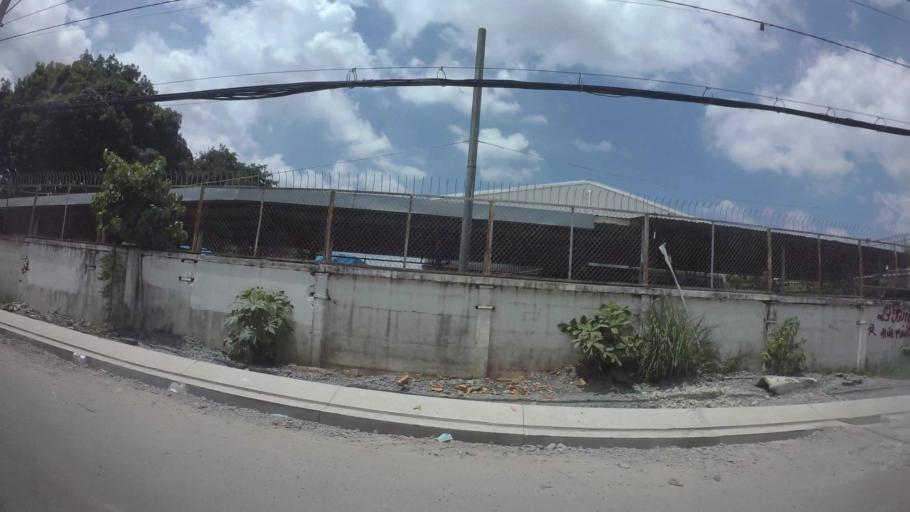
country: VN
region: Ho Chi Minh City
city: Quan Chin
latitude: 10.8316
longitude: 106.7760
